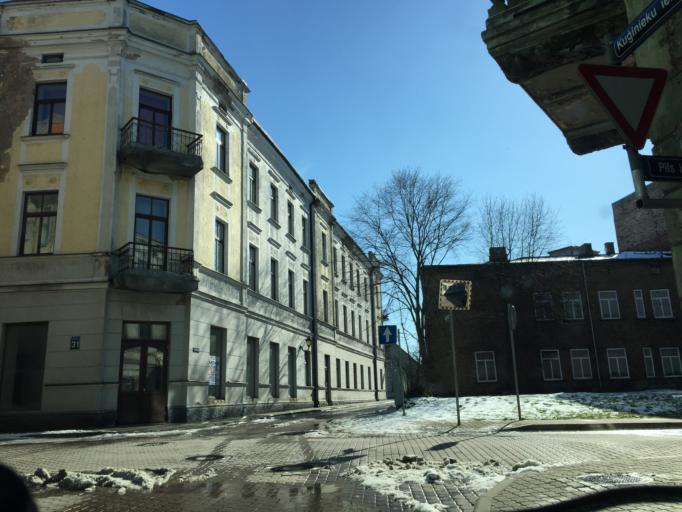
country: LV
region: Ventspils
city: Ventspils
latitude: 57.3963
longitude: 21.5624
